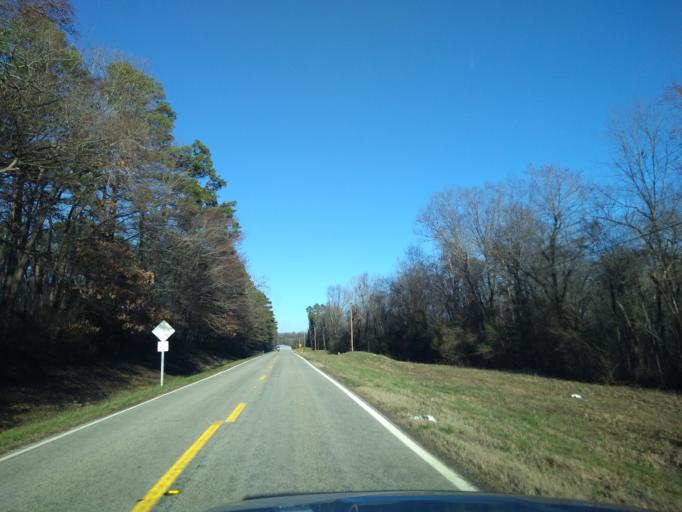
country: US
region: Arkansas
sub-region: Washington County
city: Farmington
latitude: 36.0939
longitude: -94.3598
